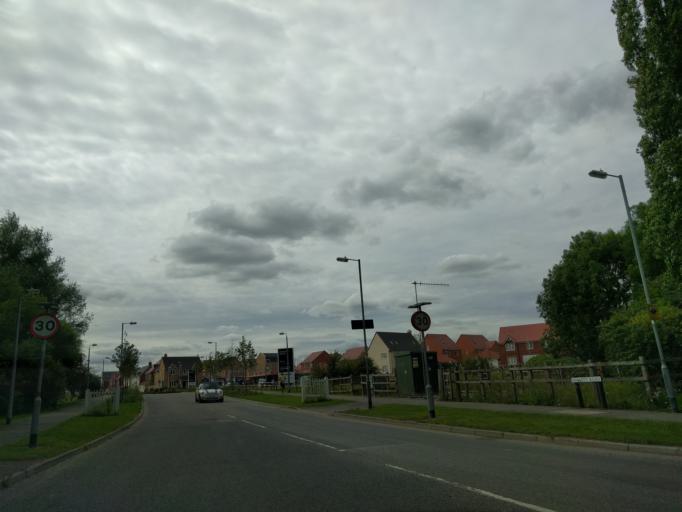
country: GB
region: England
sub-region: Essex
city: Great Dunmow
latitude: 51.8612
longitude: 0.4205
